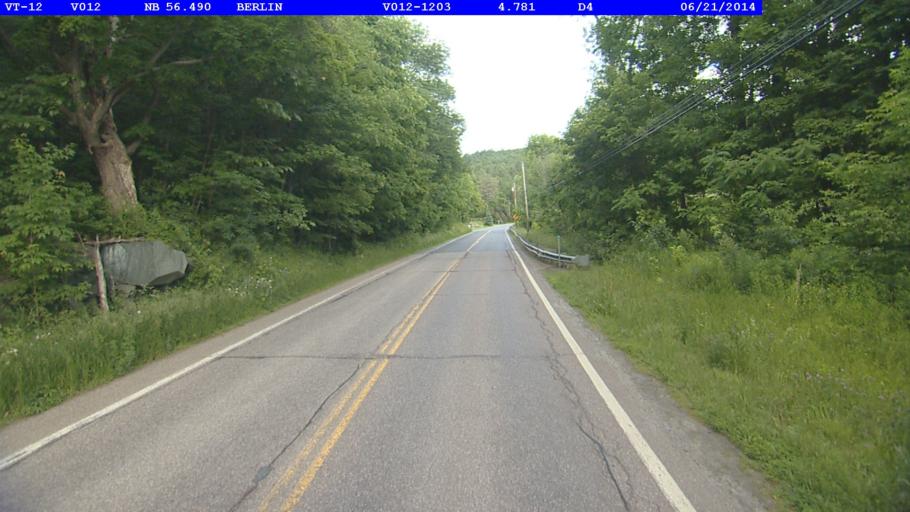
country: US
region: Vermont
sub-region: Washington County
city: Montpelier
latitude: 44.2297
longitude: -72.6104
